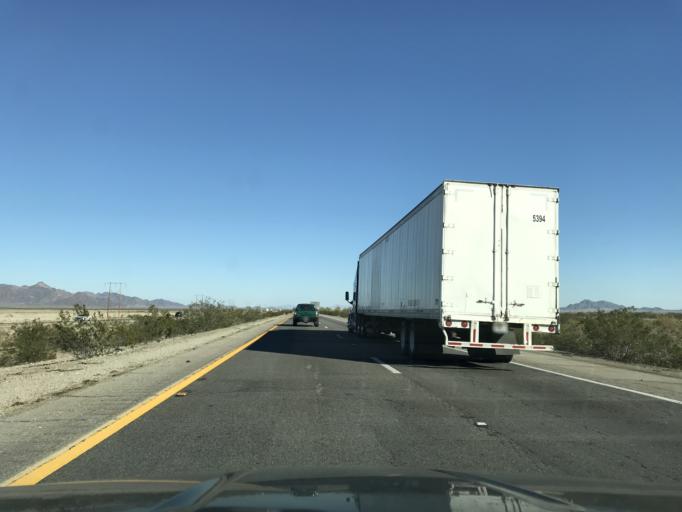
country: US
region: California
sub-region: Riverside County
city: Mesa Verde
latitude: 33.6059
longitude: -114.9722
